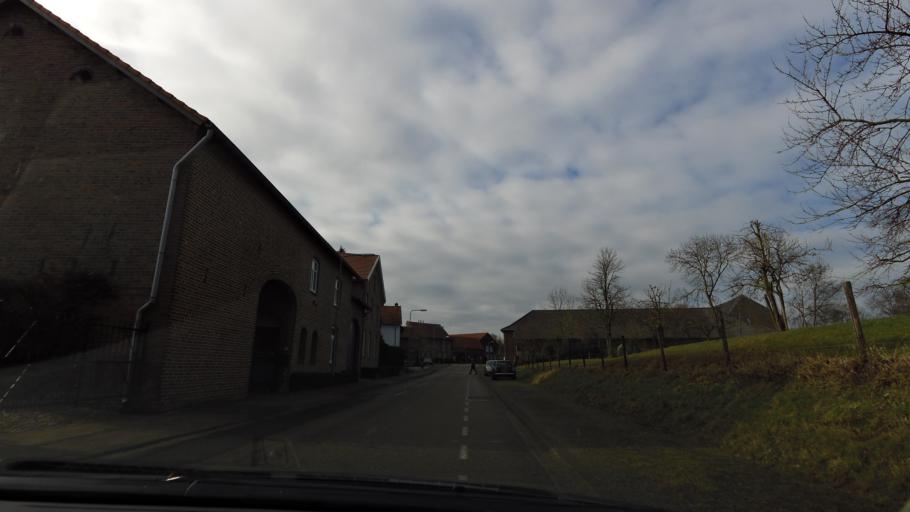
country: NL
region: Limburg
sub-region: Eijsden-Margraten
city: Margraten
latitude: 50.7976
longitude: 5.8371
